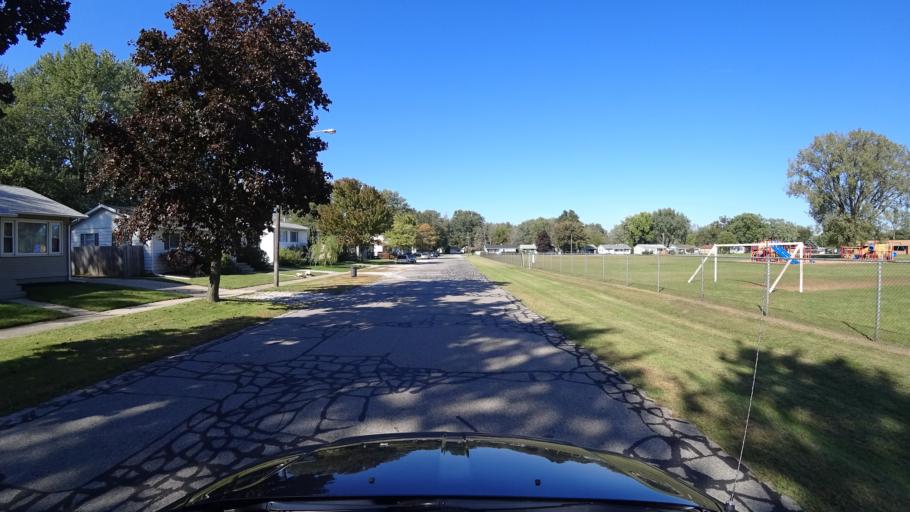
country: US
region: Indiana
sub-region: LaPorte County
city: Michigan City
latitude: 41.6954
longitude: -86.9084
